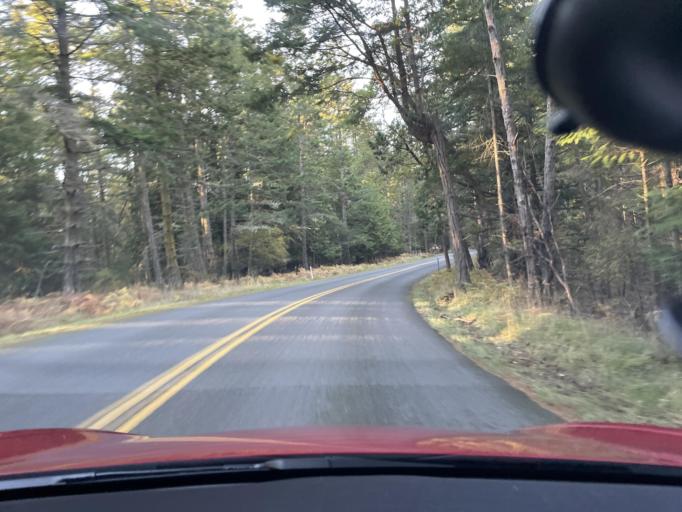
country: US
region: Washington
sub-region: San Juan County
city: Friday Harbor
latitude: 48.5338
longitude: -123.1593
